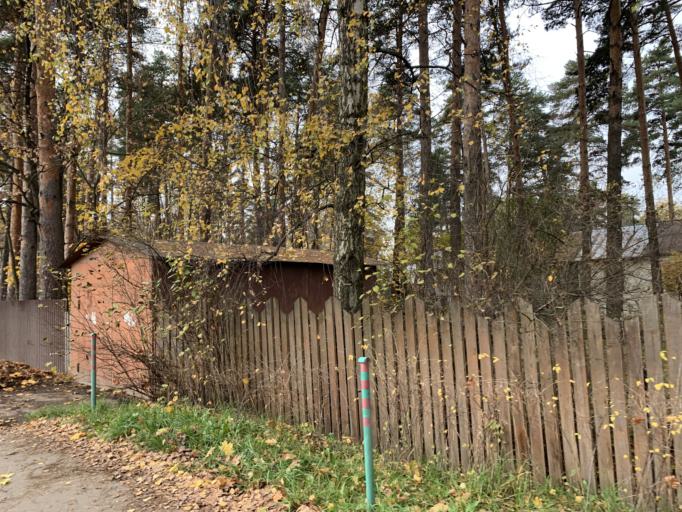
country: RU
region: Moskovskaya
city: Mamontovka
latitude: 55.9864
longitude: 37.8465
